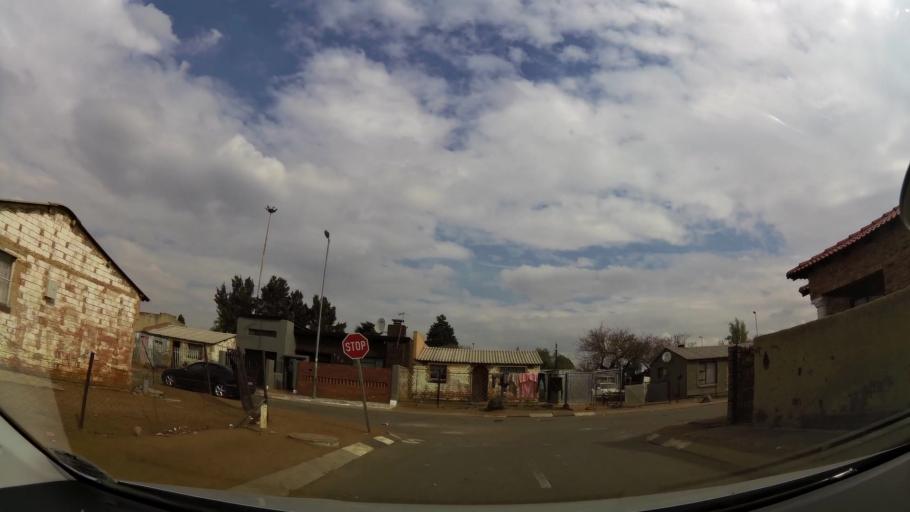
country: ZA
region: Gauteng
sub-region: City of Johannesburg Metropolitan Municipality
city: Soweto
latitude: -26.2703
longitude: 27.8580
